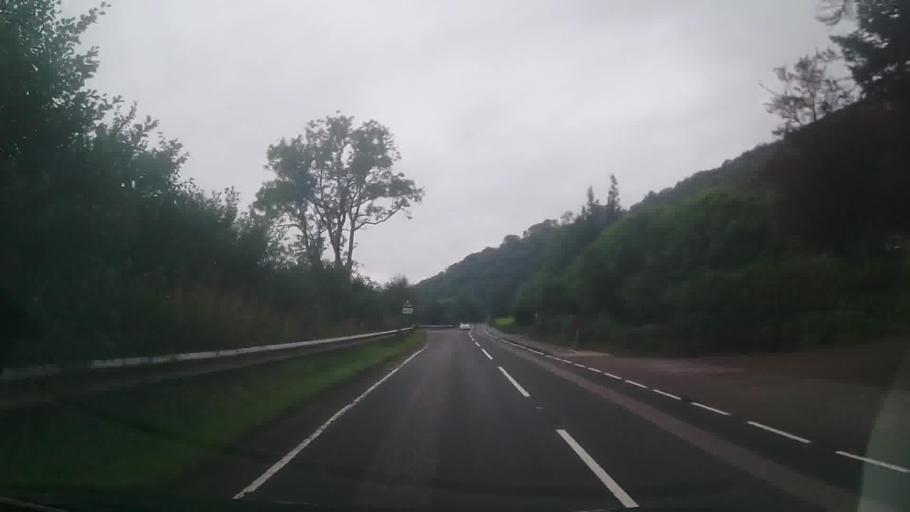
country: GB
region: Scotland
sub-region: Highland
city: Fort William
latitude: 56.7008
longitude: -5.2011
